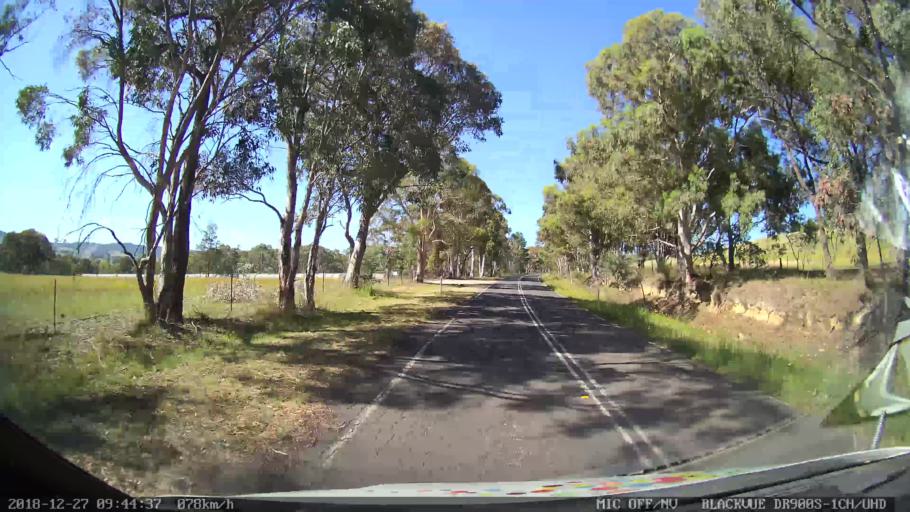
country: AU
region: New South Wales
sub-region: Lithgow
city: Portland
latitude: -33.3175
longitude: 149.9918
